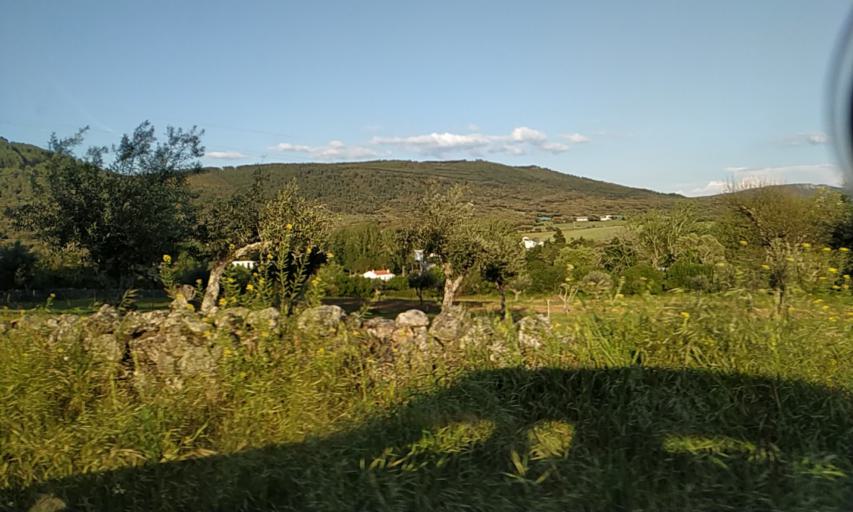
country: PT
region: Portalegre
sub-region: Marvao
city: Marvao
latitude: 39.3688
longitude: -7.3887
